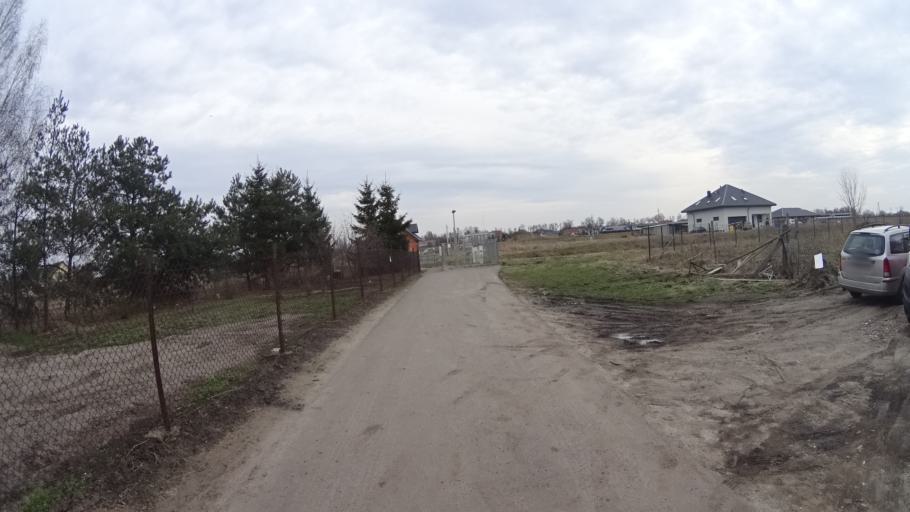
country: PL
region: Masovian Voivodeship
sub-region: Powiat warszawski zachodni
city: Jozefow
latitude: 52.2013
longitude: 20.6935
